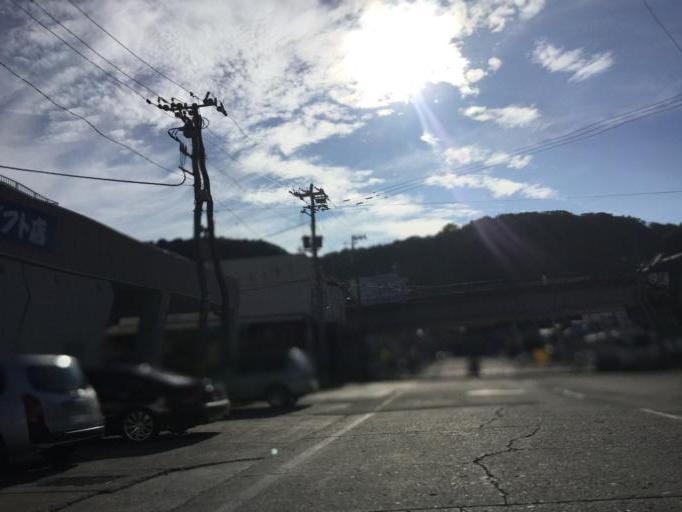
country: JP
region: Hokkaido
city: Wakkanai
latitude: 45.4096
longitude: 141.6769
